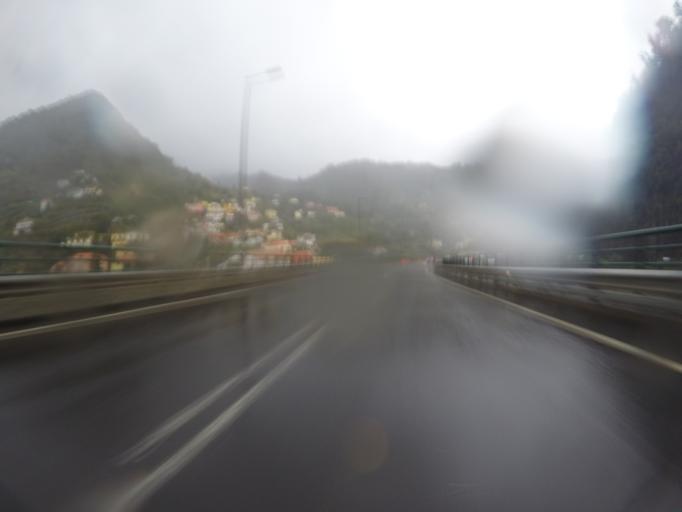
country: PT
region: Madeira
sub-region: Machico
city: Machico
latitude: 32.7346
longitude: -16.7953
